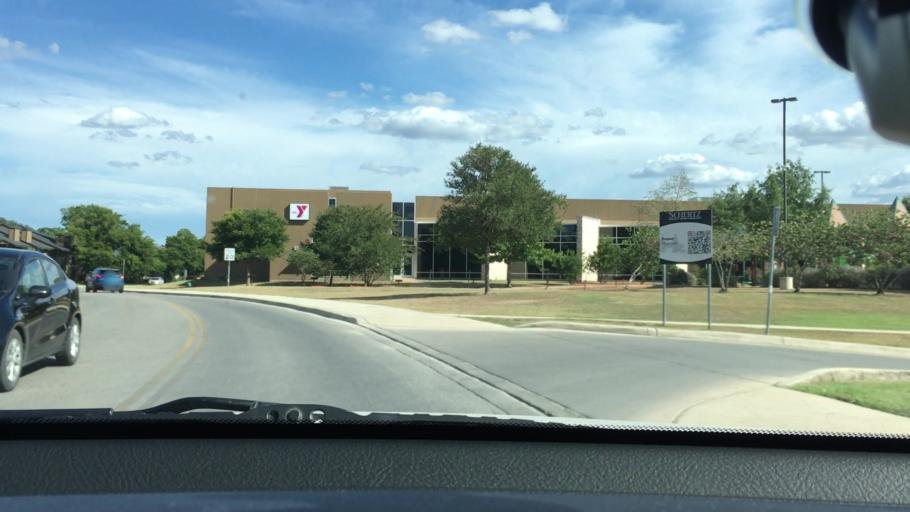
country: US
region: Texas
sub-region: Guadalupe County
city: Schertz
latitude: 29.5612
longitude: -98.2655
